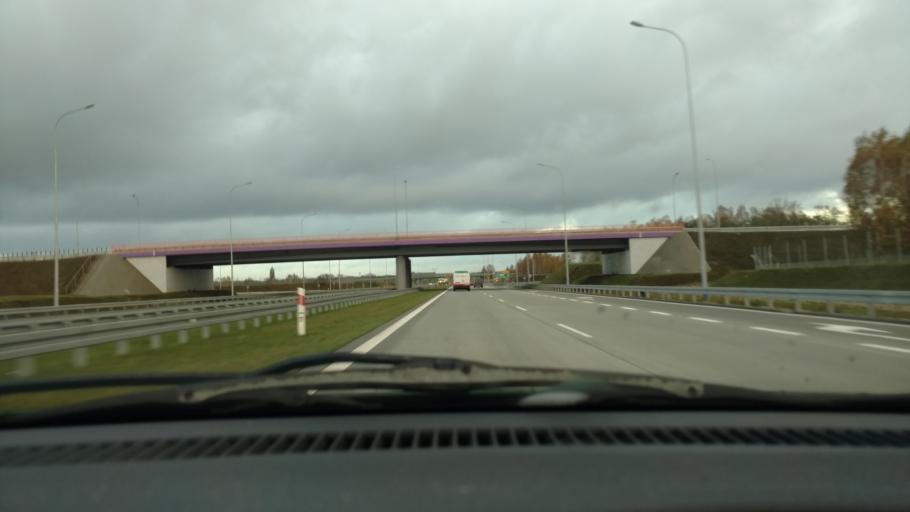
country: PL
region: Lodz Voivodeship
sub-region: Powiat lodzki wschodni
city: Brojce
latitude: 51.6750
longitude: 19.5897
